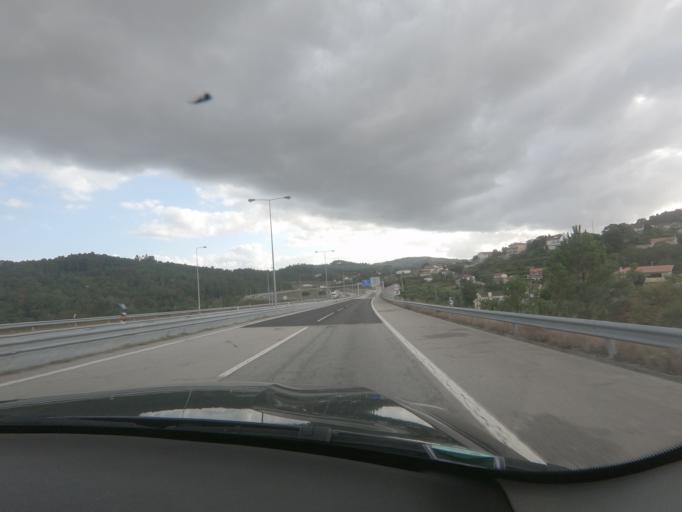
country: PT
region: Viseu
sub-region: Castro Daire
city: Castro Daire
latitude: 40.9052
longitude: -7.9083
